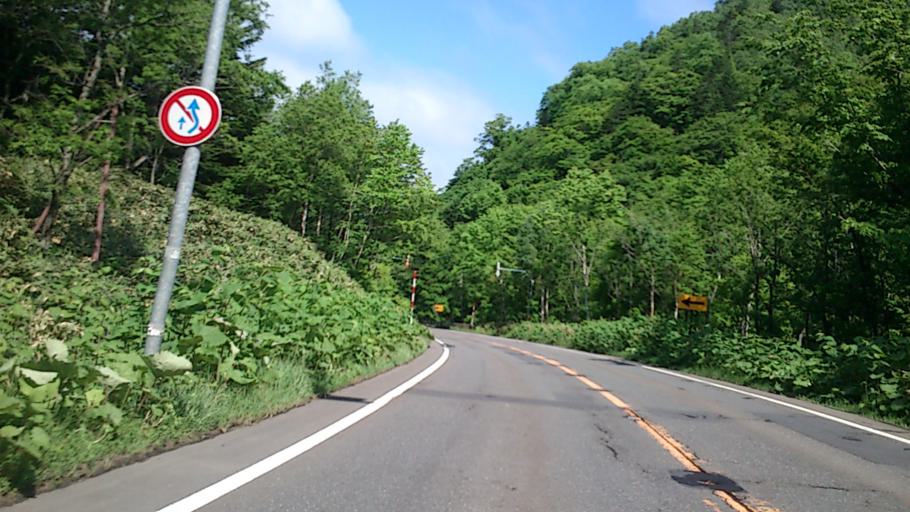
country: JP
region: Hokkaido
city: Shiraoi
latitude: 42.7172
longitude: 141.2243
